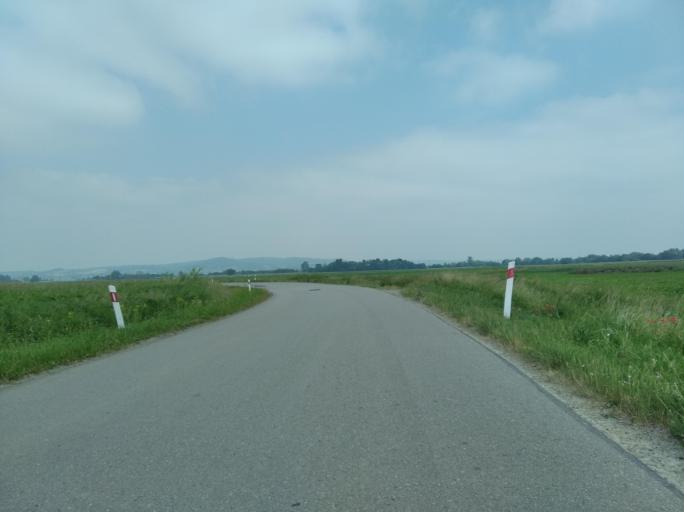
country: PL
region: Subcarpathian Voivodeship
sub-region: Powiat sanocki
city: Besko
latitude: 49.6103
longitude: 21.9555
